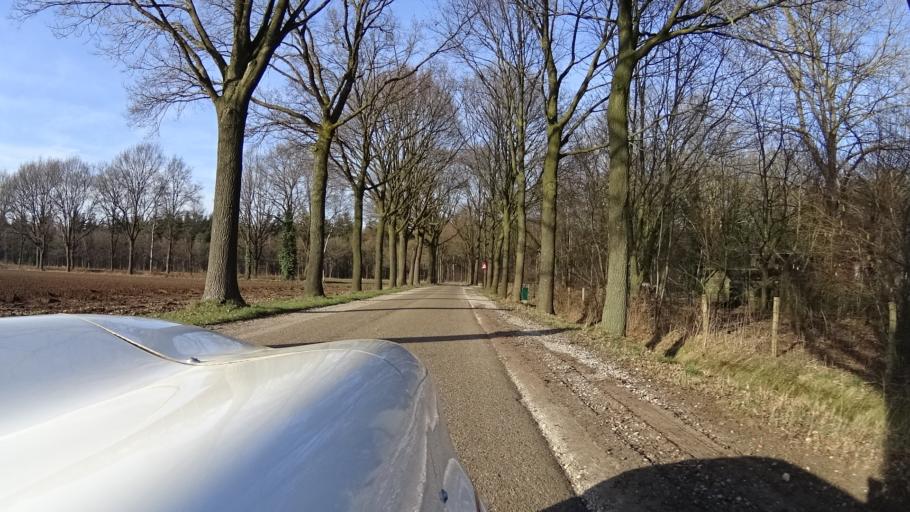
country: NL
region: North Brabant
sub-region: Gemeente Veghel
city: Erp
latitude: 51.5675
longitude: 5.6350
